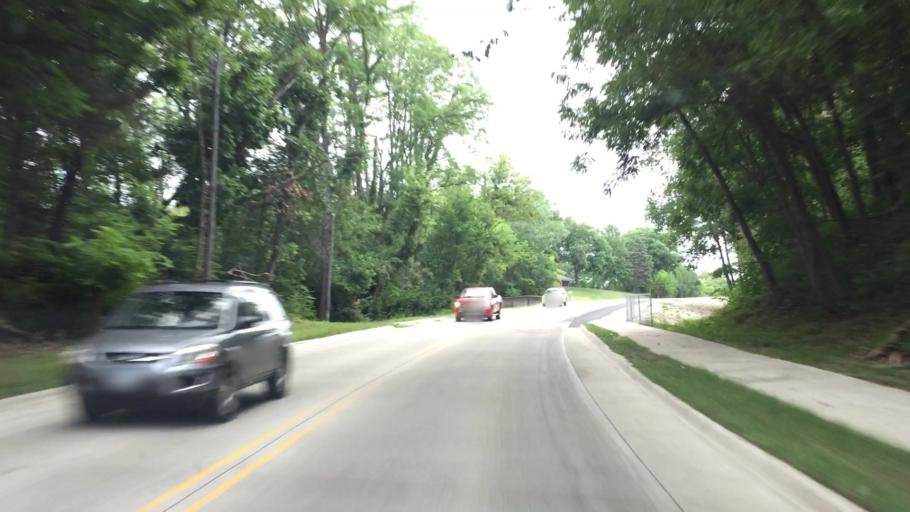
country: US
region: Iowa
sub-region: Lee County
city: Fort Madison
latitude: 40.6385
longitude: -91.3242
